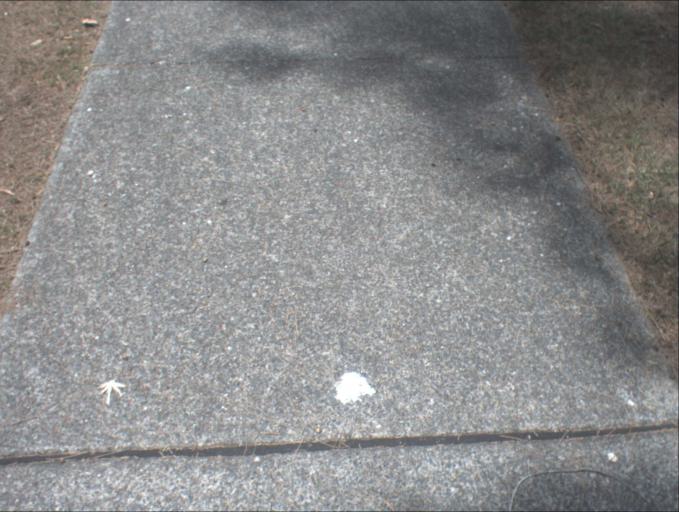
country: AU
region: Queensland
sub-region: Logan
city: Beenleigh
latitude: -27.7001
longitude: 153.1695
